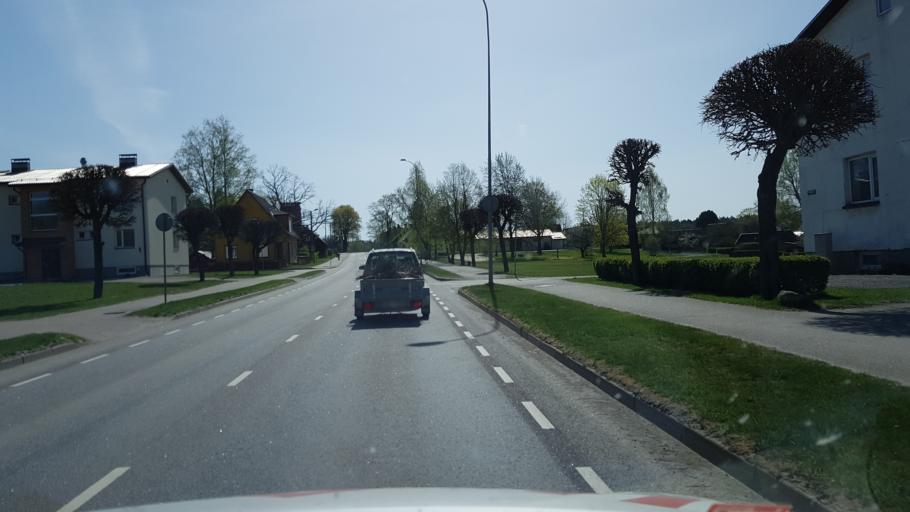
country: EE
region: Valgamaa
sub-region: Torva linn
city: Torva
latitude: 58.0010
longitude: 25.9265
